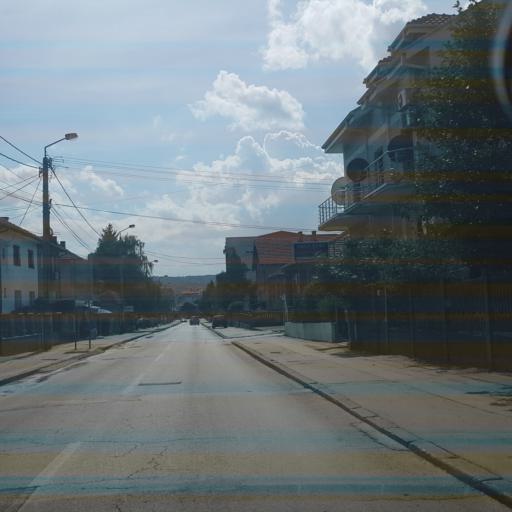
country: RS
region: Central Serbia
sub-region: Nisavski Okrug
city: Nis
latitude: 43.3310
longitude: 21.9077
